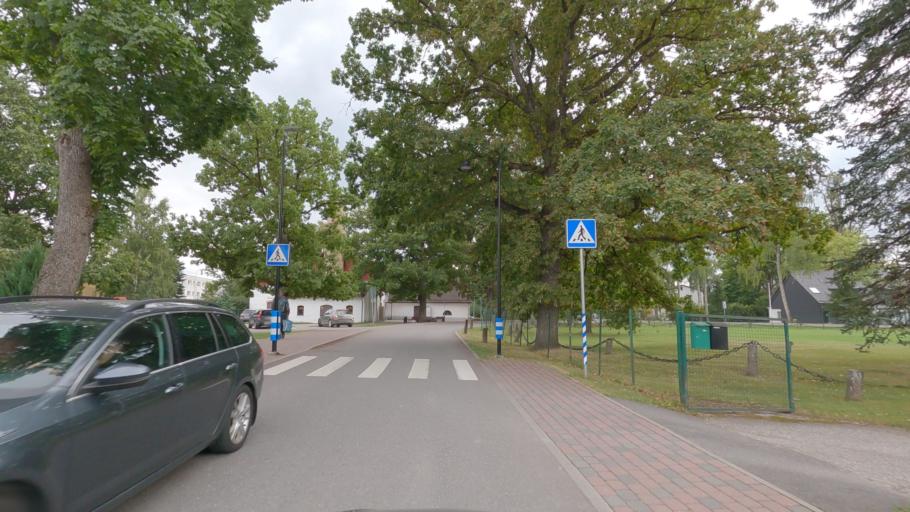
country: EE
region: Raplamaa
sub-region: Kohila vald
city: Kohila
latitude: 59.1735
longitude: 24.7508
